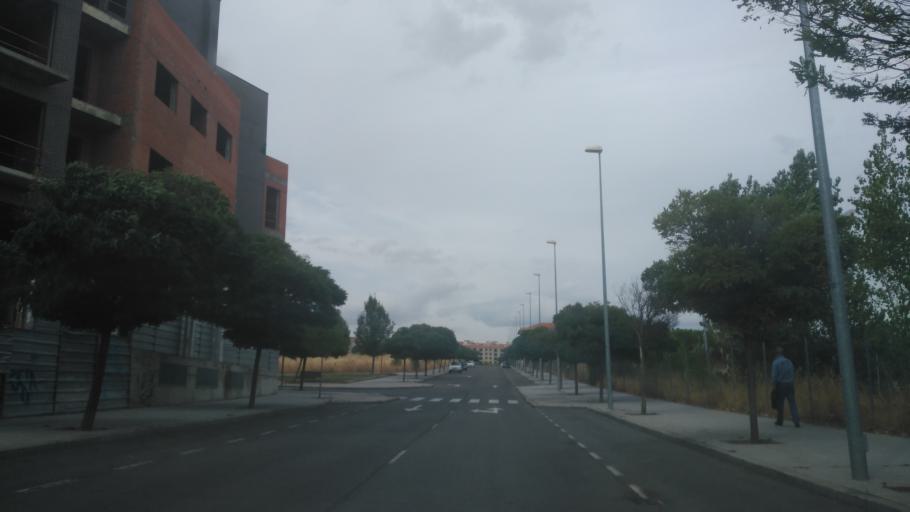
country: ES
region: Castille and Leon
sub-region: Provincia de Salamanca
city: Salamanca
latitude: 40.9686
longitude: -5.6815
